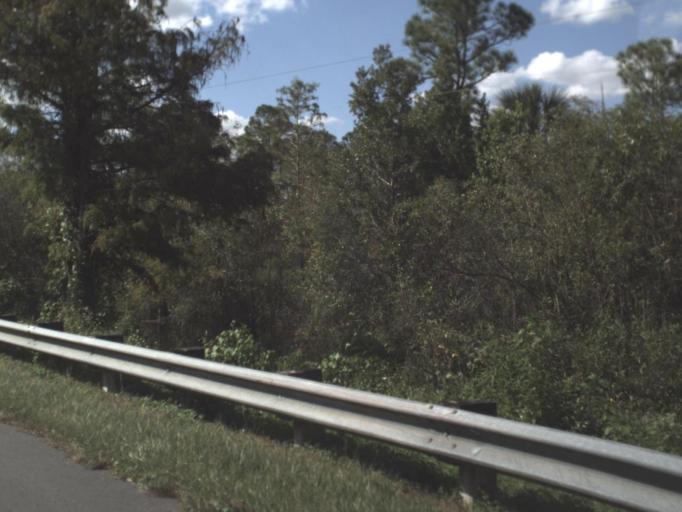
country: US
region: Florida
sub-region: Collier County
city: Marco
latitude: 25.8775
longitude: -81.2356
